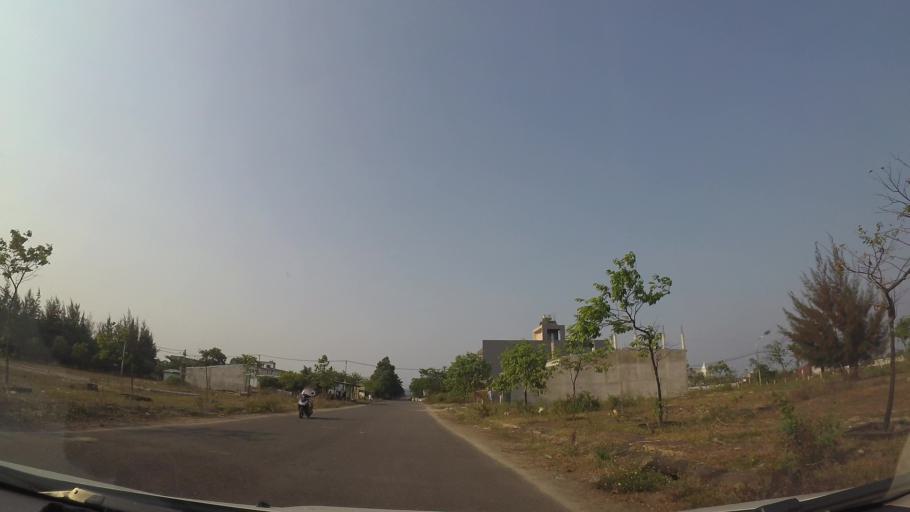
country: VN
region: Da Nang
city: Ngu Hanh Son
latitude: 15.9597
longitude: 108.2568
